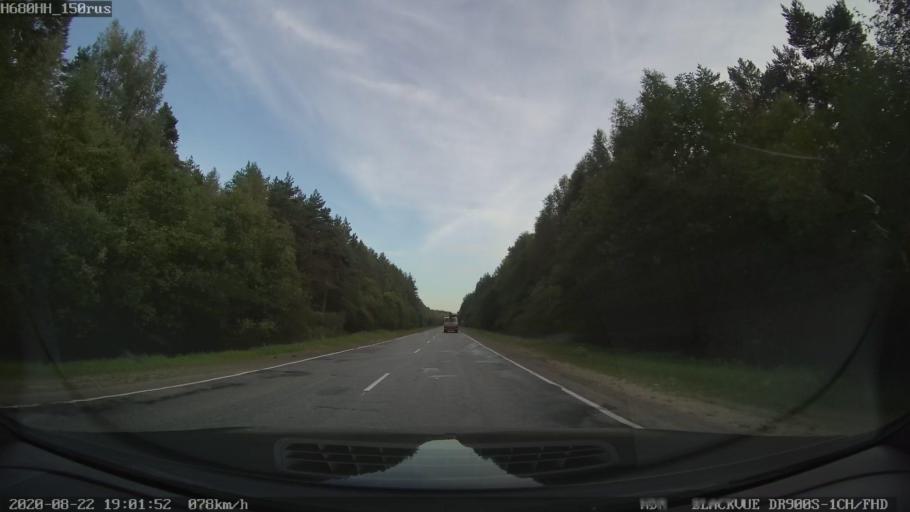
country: RU
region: Tverskaya
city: Vasil'yevskiy Mokh
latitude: 57.1147
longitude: 36.1172
